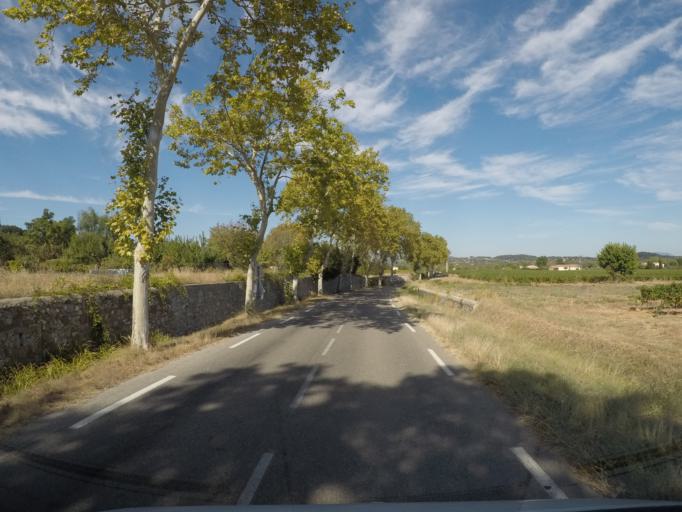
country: FR
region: Languedoc-Roussillon
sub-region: Departement du Gard
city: Boisset-et-Gaujac
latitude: 44.0288
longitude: 3.9990
